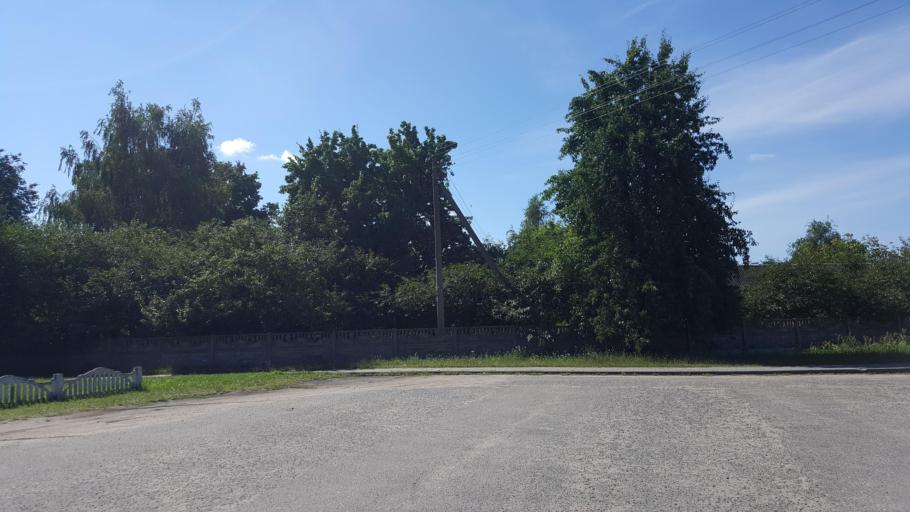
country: BY
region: Brest
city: Charnawchytsy
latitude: 52.2742
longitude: 23.7684
